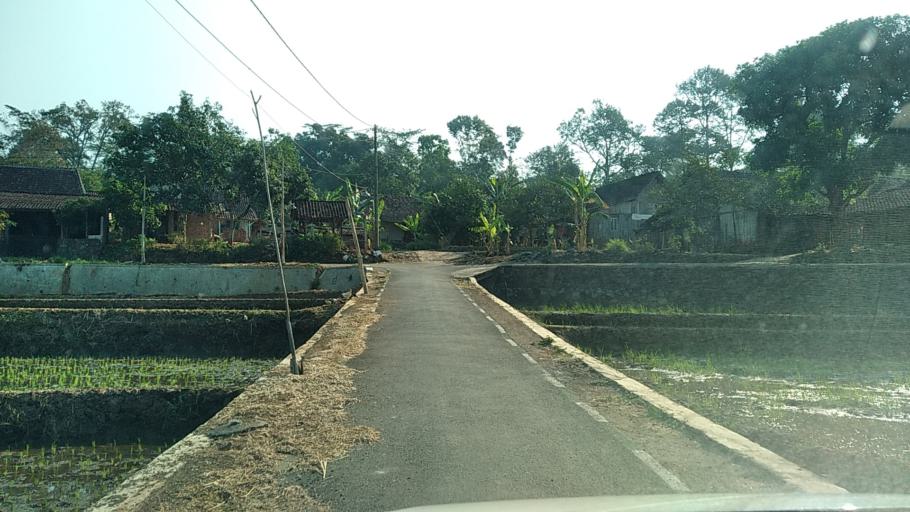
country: ID
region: Central Java
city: Semarang
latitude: -7.0235
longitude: 110.2899
